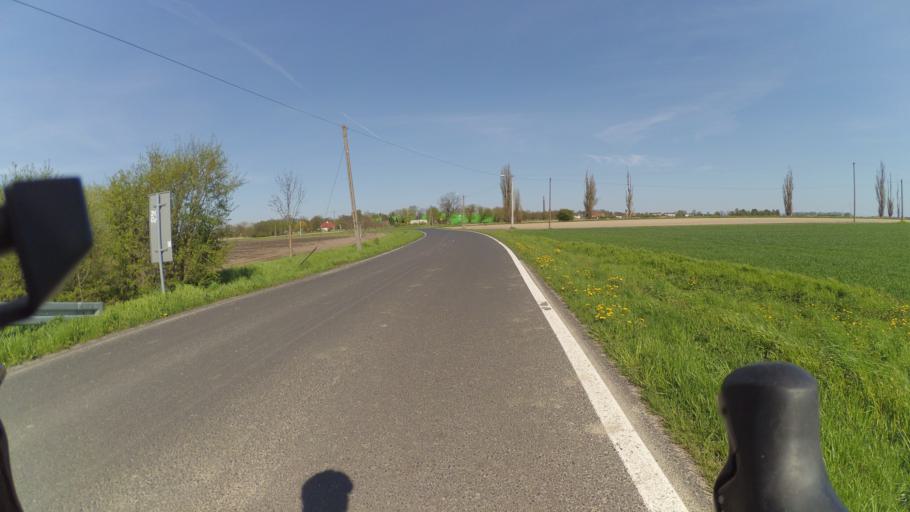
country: PL
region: Masovian Voivodeship
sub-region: Powiat warszawski zachodni
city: Leszno
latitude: 52.2526
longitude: 20.5686
